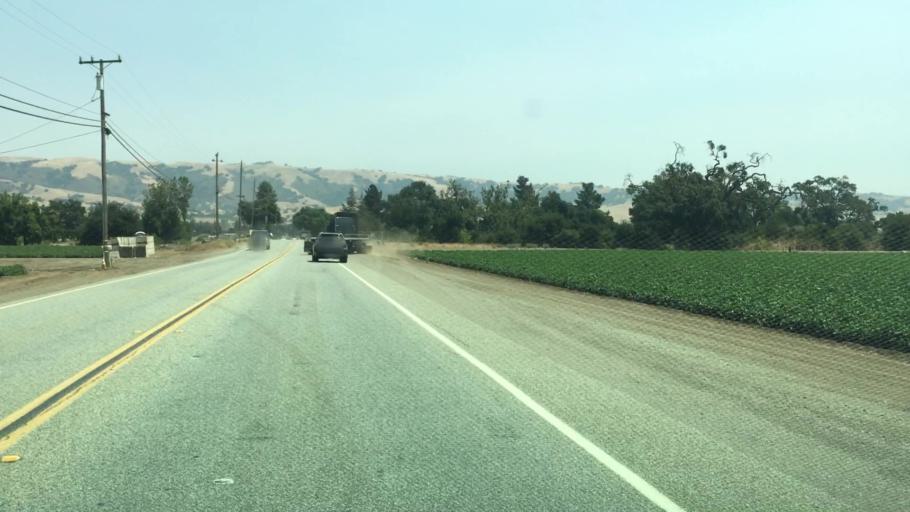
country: US
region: California
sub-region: Santa Clara County
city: Gilroy
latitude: 37.0305
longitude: -121.5454
